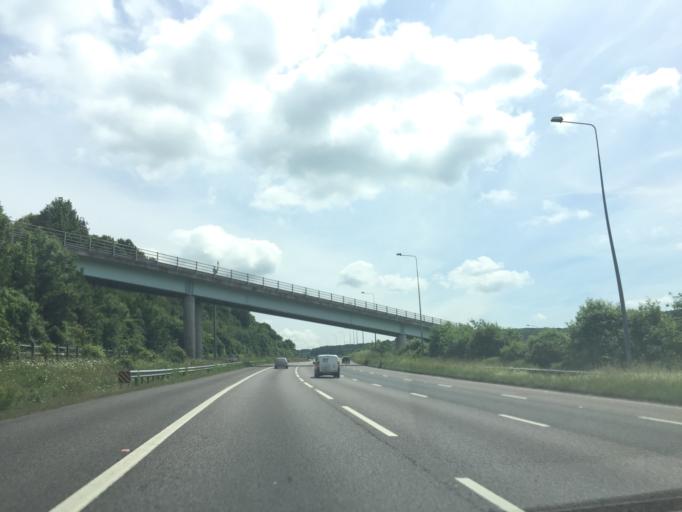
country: GB
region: England
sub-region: Medway
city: Rochester
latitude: 51.3574
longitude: 0.4946
